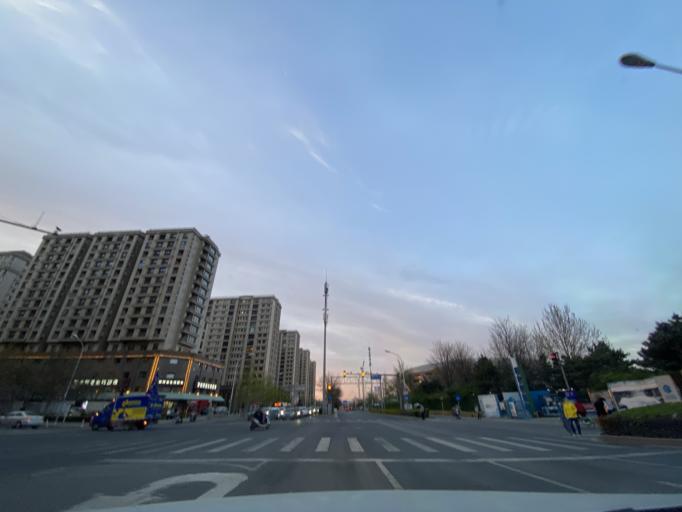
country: CN
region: Beijing
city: Qinghe
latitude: 40.0160
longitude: 116.3686
